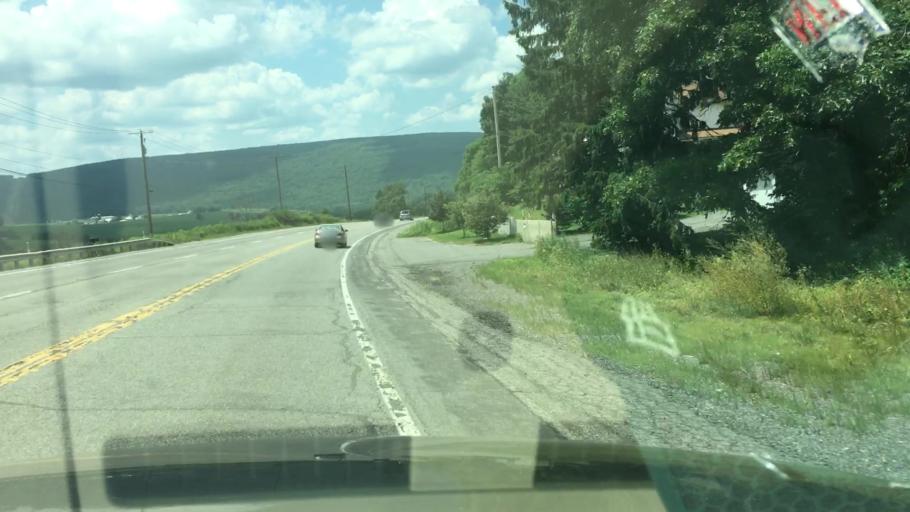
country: US
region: Pennsylvania
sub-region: Schuylkill County
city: Ashland
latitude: 40.7236
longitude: -76.3860
